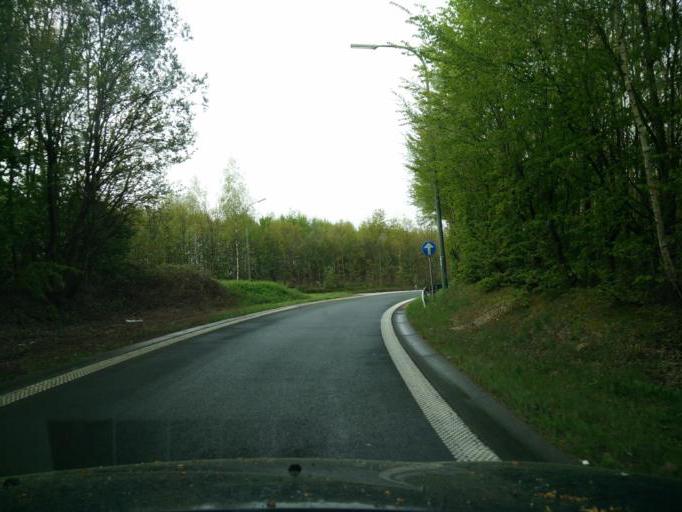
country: BE
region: Flanders
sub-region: Provincie Vlaams-Brabant
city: Halle
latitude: 50.7262
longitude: 4.2585
